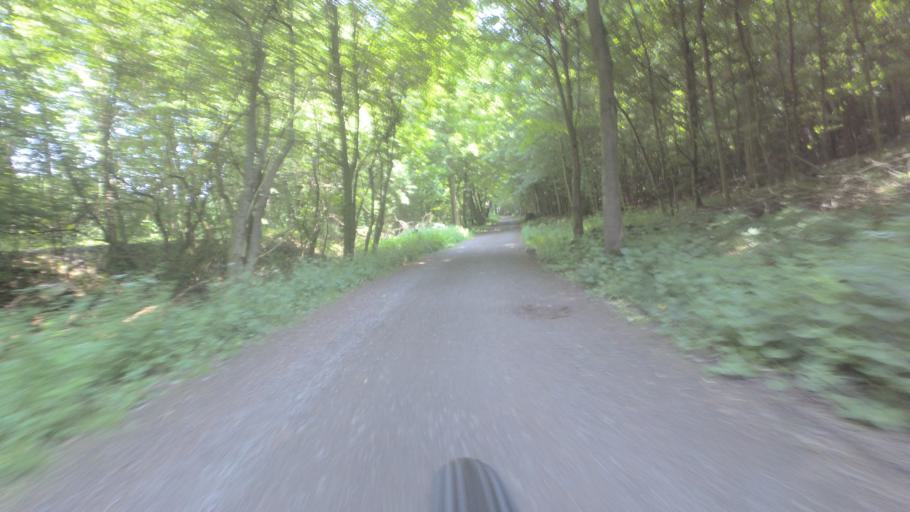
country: DE
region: Saxony-Anhalt
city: Rieder
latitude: 51.7256
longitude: 11.1930
